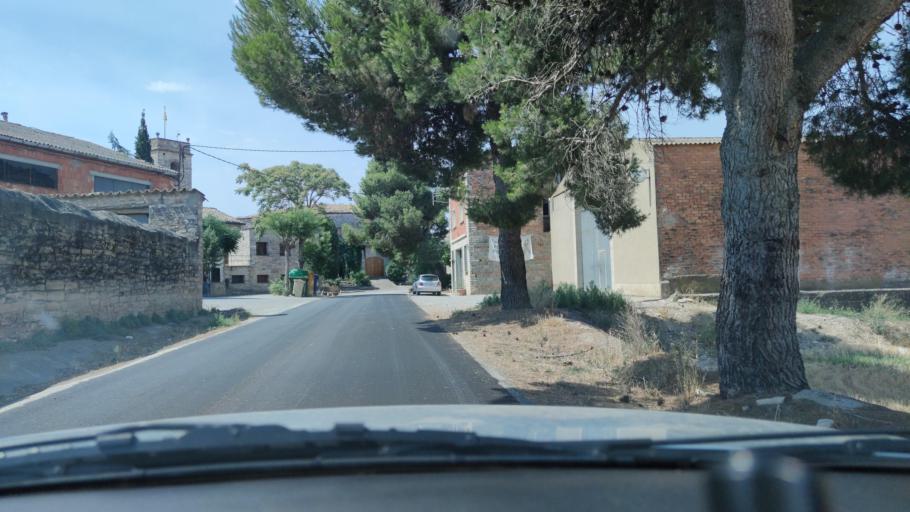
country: ES
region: Catalonia
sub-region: Provincia de Lleida
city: Ivorra
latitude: 41.7636
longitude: 1.3247
